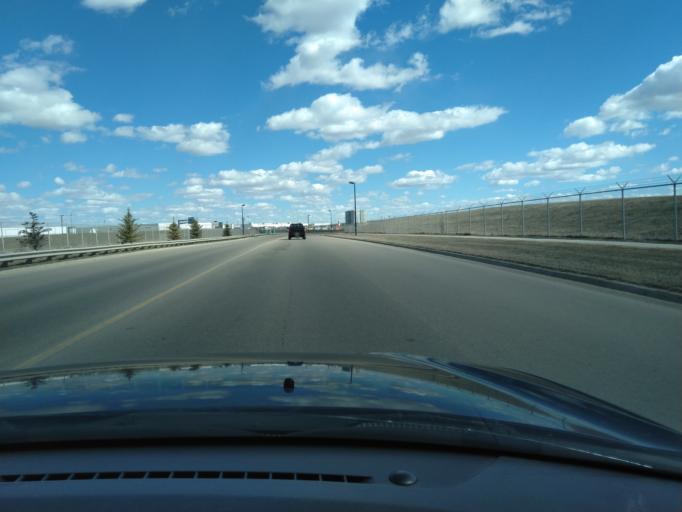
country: CA
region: Alberta
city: Calgary
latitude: 51.1376
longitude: -114.0244
